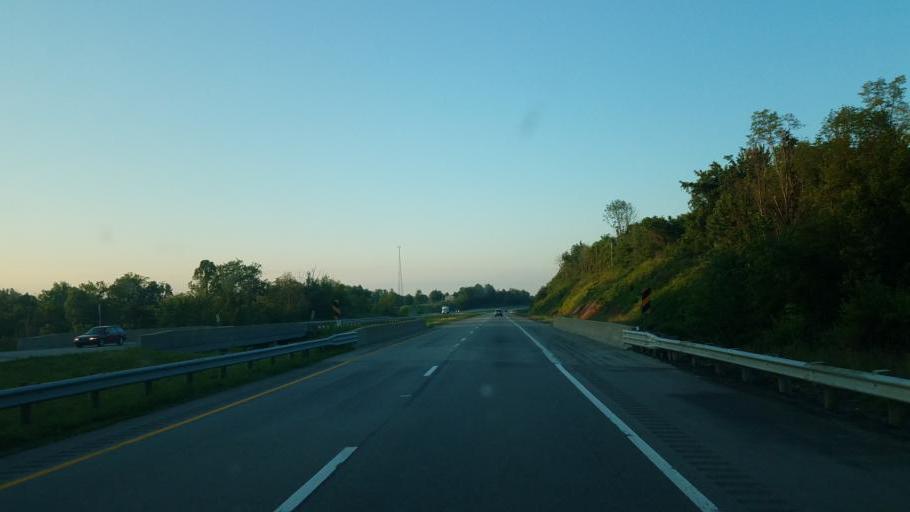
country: US
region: Ohio
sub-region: Washington County
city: Devola
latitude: 39.5693
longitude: -81.4521
